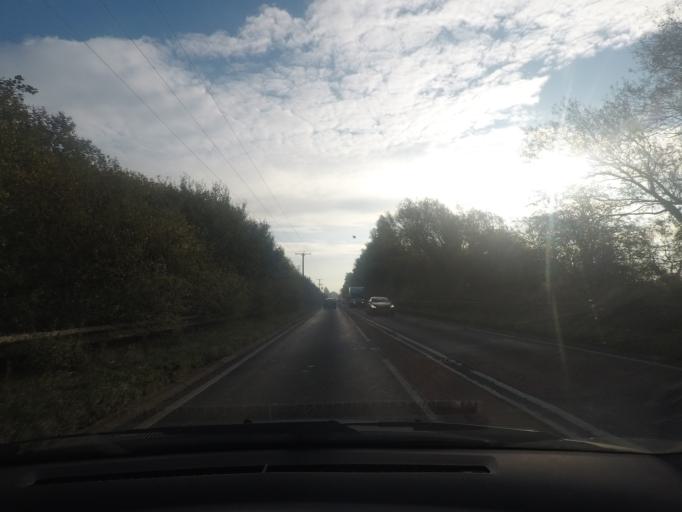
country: GB
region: England
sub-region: East Riding of Yorkshire
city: Wilberfoss
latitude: 53.9477
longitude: -0.8948
